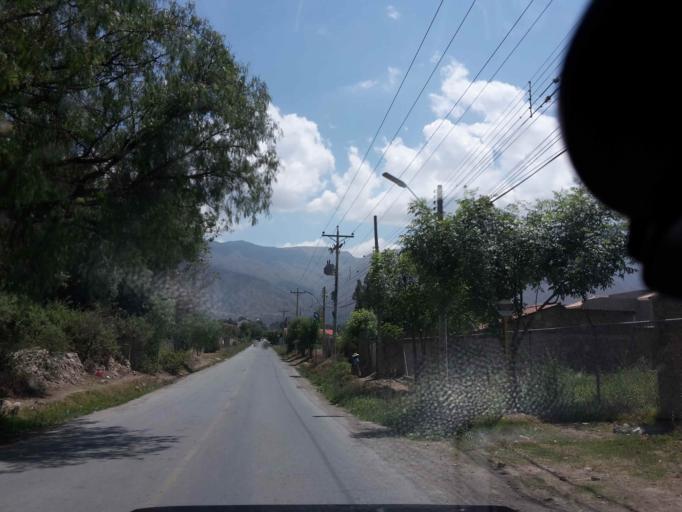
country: BO
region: Cochabamba
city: Cochabamba
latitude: -17.3554
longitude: -66.2270
